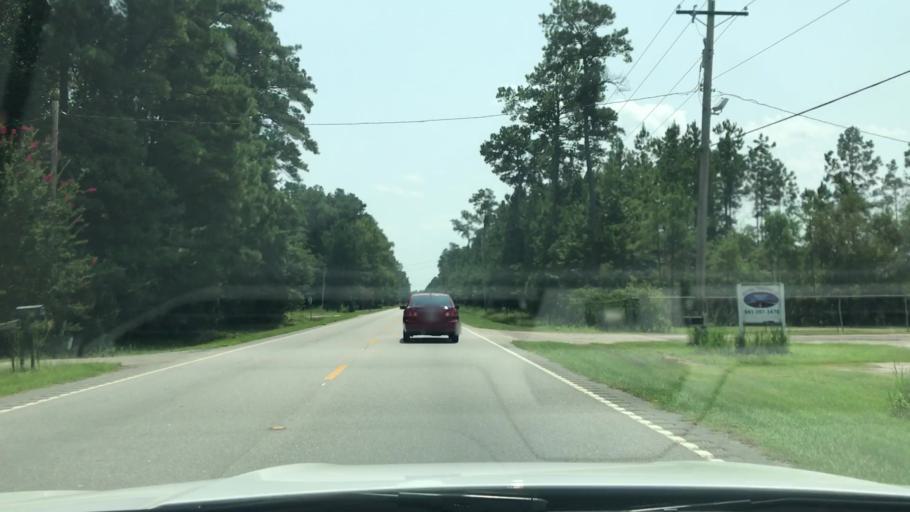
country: US
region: South Carolina
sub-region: Horry County
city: Conway
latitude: 33.7862
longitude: -79.0754
